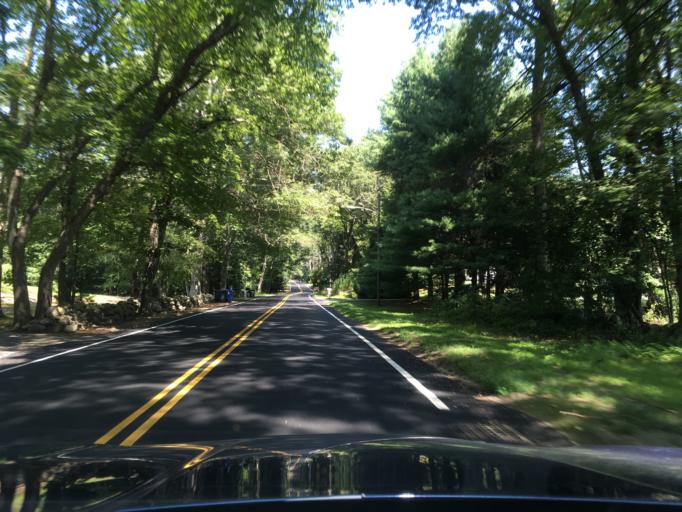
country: US
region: Rhode Island
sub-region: Kent County
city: West Warwick
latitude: 41.6467
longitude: -71.5219
